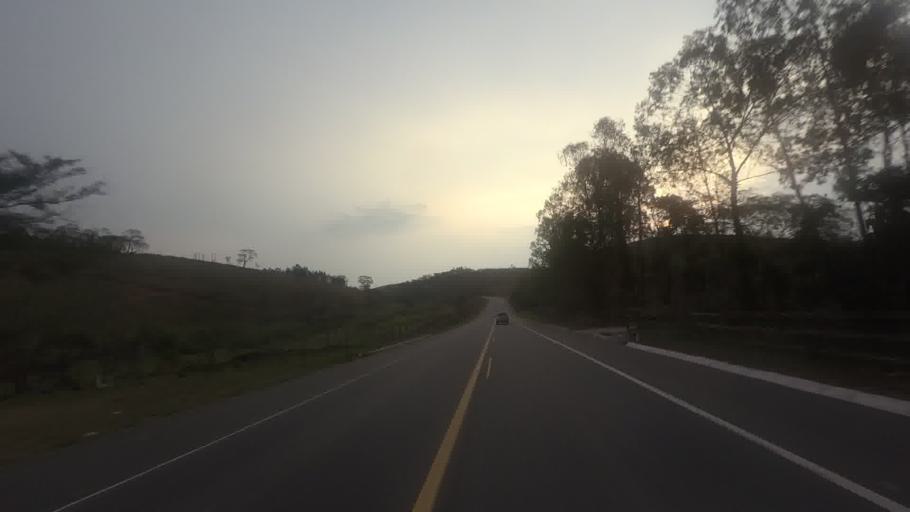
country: BR
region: Rio de Janeiro
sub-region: Carmo
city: Carmo
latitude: -21.7789
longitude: -42.5382
